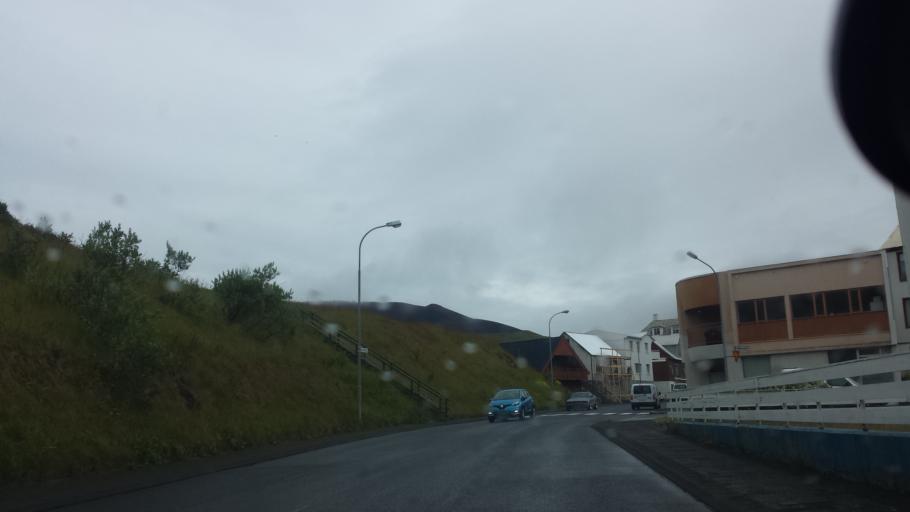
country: IS
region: South
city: Vestmannaeyjar
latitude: 63.4421
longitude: -20.2672
